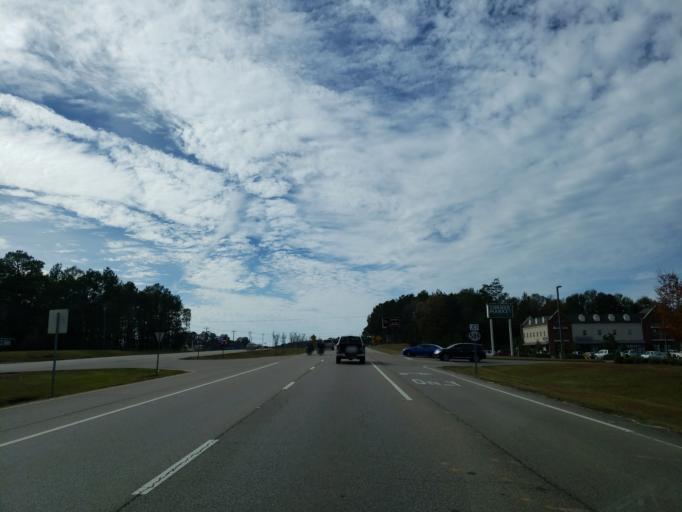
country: US
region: Mississippi
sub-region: Lamar County
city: West Hattiesburg
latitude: 31.3136
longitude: -89.4657
